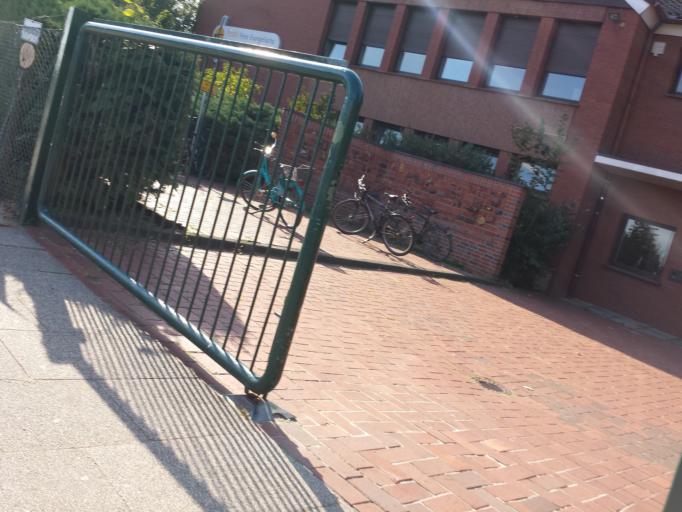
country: DE
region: Bremen
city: Bremen
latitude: 53.0511
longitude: 8.8480
